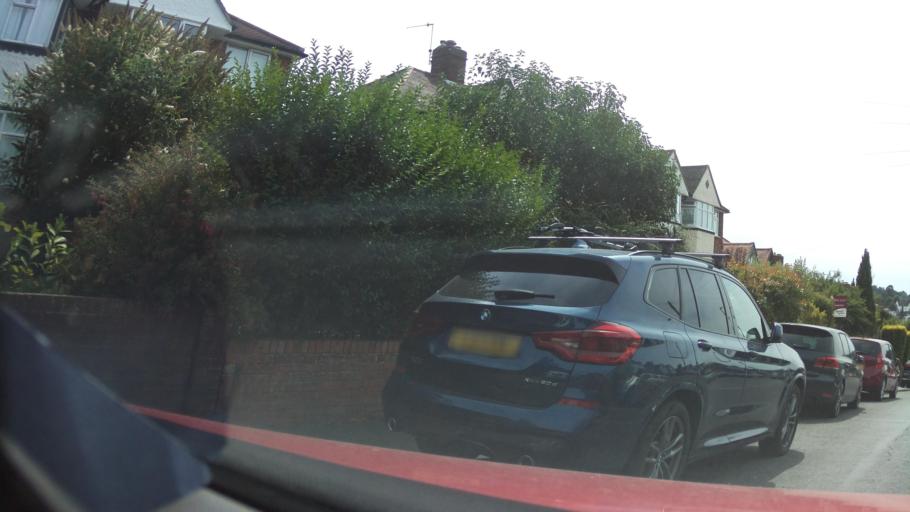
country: GB
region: England
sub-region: Surrey
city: Dorking
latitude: 51.2366
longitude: -0.3360
